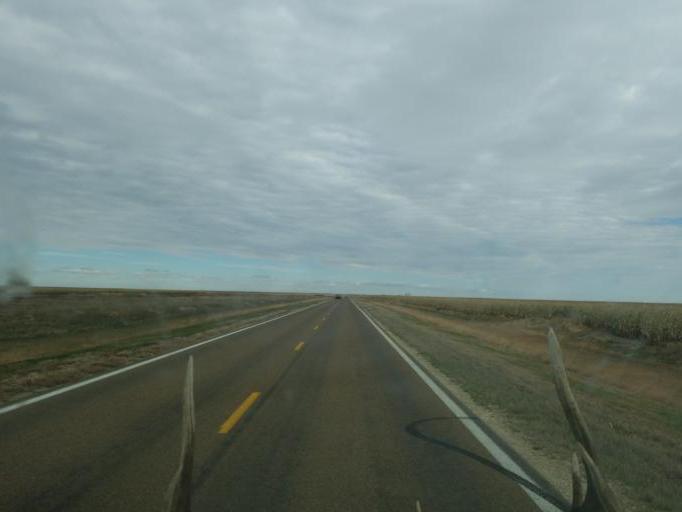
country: US
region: Kansas
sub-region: Logan County
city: Oakley
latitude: 39.0674
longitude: -101.2212
